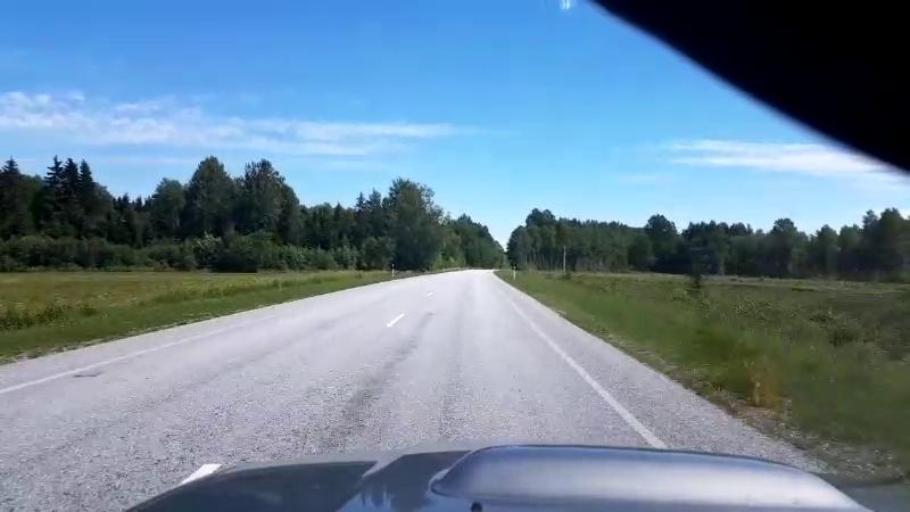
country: EE
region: Laeaene-Virumaa
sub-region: Rakke vald
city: Rakke
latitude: 58.9617
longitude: 26.1600
